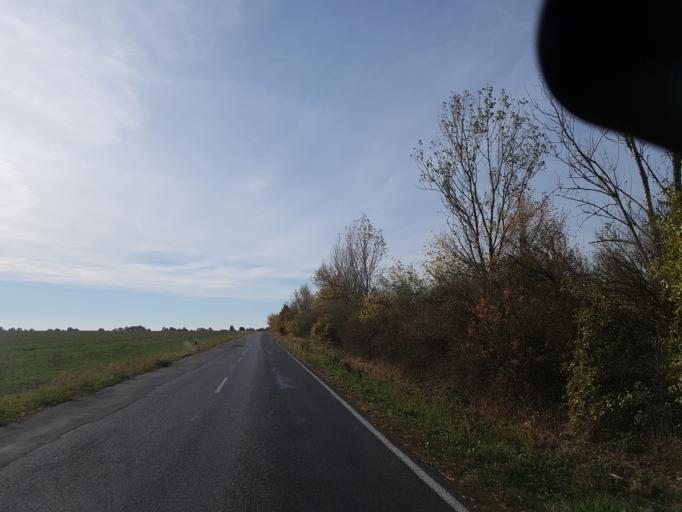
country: DE
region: Brandenburg
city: Ihlow
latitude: 51.9171
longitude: 13.2253
